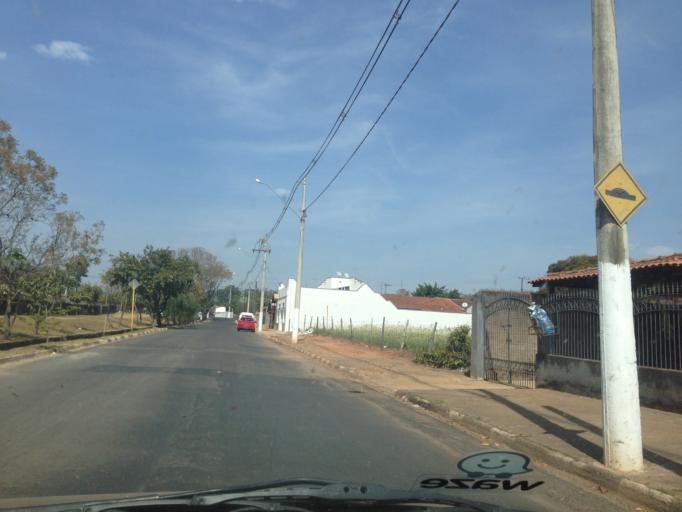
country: BR
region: Sao Paulo
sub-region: Casa Branca
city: Casa Branca
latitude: -21.7757
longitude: -47.0905
